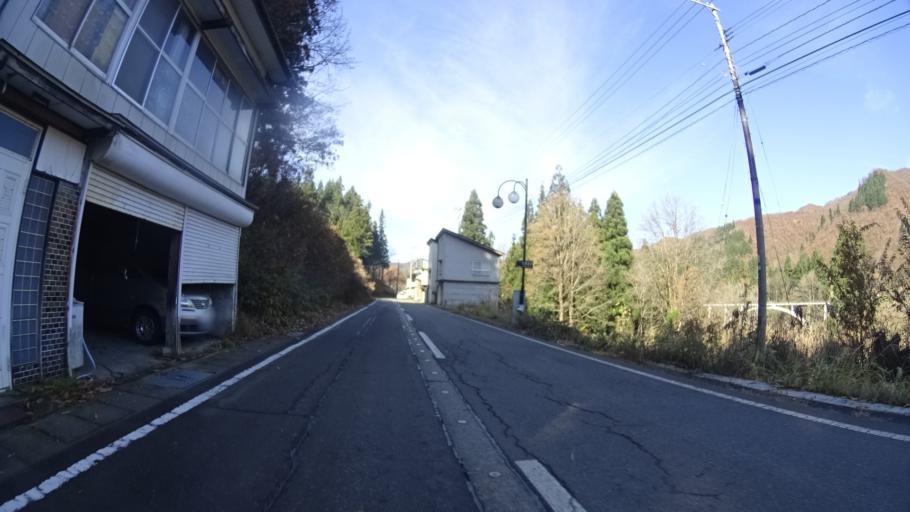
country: JP
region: Niigata
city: Muikamachi
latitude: 37.1949
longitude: 139.0784
